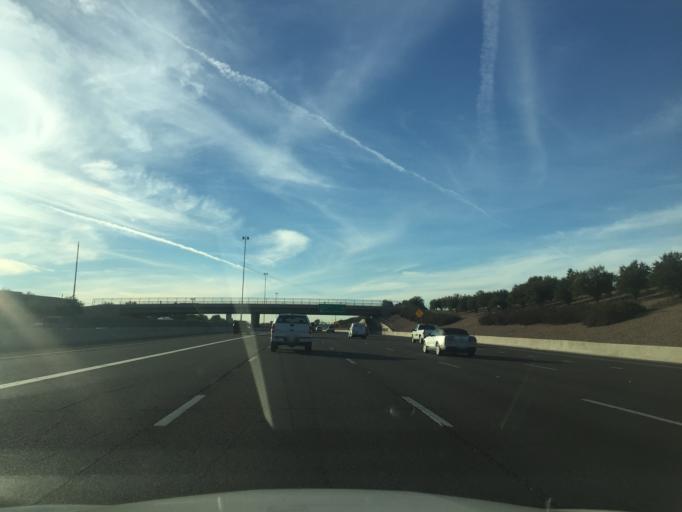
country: US
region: Arizona
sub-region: Maricopa County
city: Gilbert
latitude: 33.3864
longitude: -111.7952
